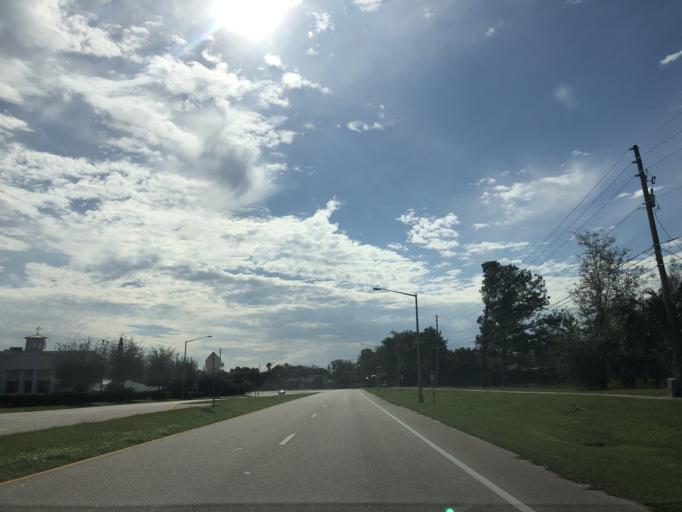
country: US
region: Florida
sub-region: Orange County
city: Bay Hill
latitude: 28.4842
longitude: -81.4922
